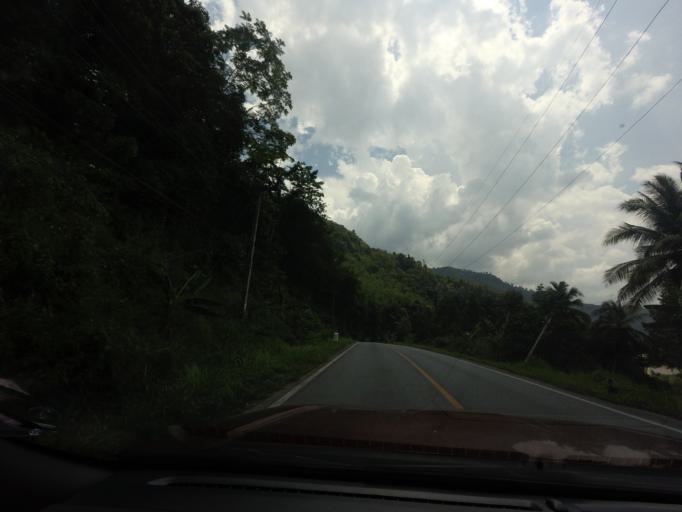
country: TH
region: Yala
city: Than To
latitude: 5.9879
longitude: 101.1936
